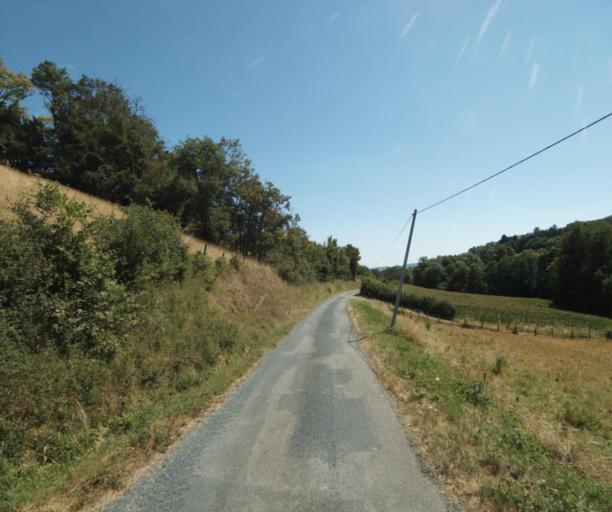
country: FR
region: Rhone-Alpes
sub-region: Departement du Rhone
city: Montrottier
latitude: 45.7901
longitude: 4.5045
